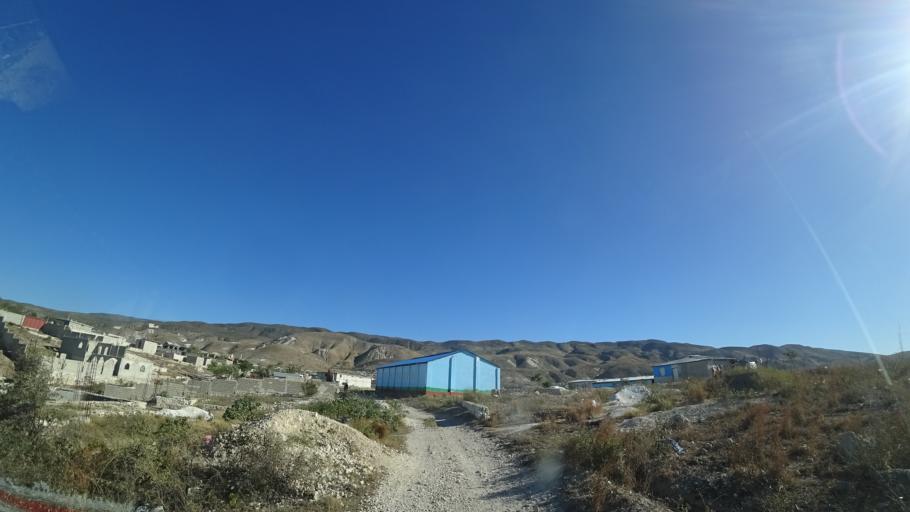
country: HT
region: Ouest
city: Cabaret
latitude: 18.6853
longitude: -72.3220
